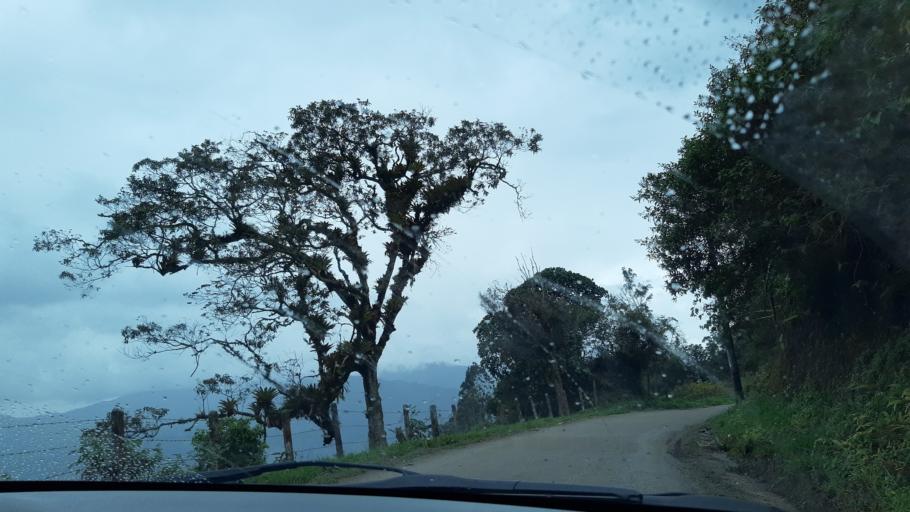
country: CO
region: Boyaca
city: Chivor
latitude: 4.9706
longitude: -73.3183
